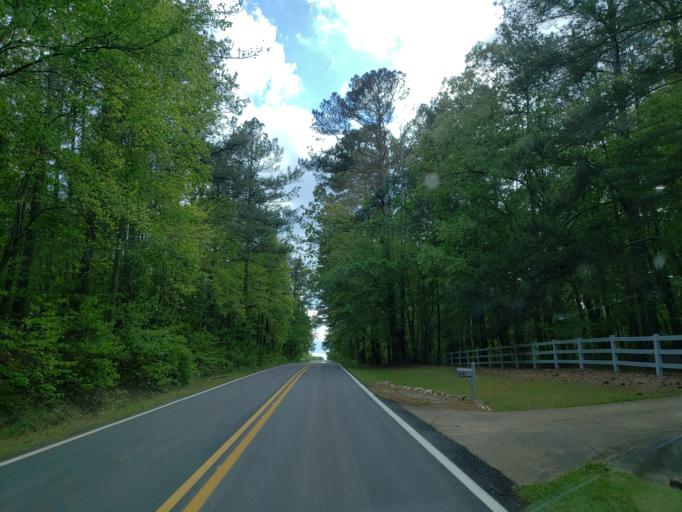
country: US
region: Georgia
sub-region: Carroll County
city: Mount Zion
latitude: 33.6780
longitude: -85.2221
